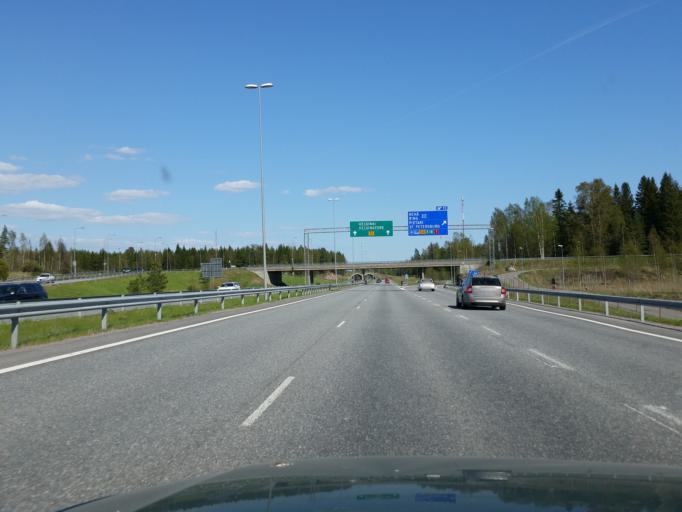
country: FI
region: Uusimaa
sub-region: Helsinki
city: Kirkkonummi
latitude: 60.1371
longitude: 24.5308
